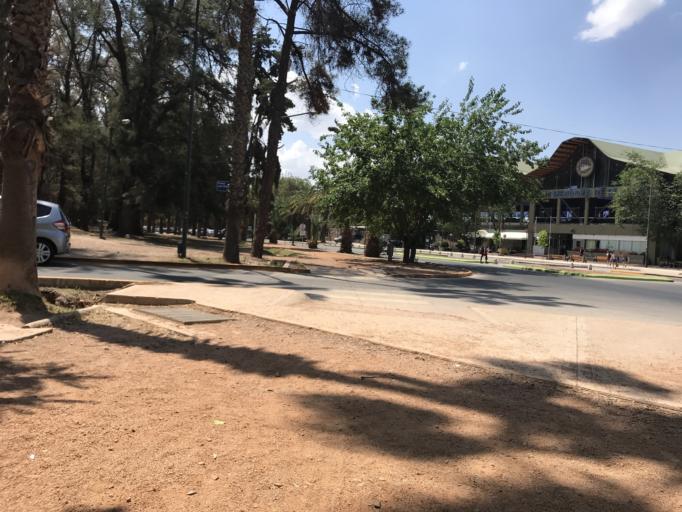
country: AR
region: Mendoza
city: Mendoza
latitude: -32.8942
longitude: -68.8675
